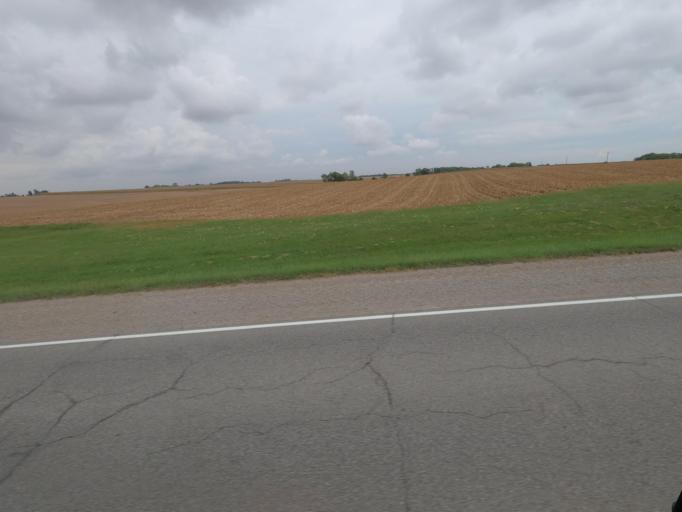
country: US
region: Iowa
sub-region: Wapello County
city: Ottumwa
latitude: 40.9722
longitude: -92.2365
